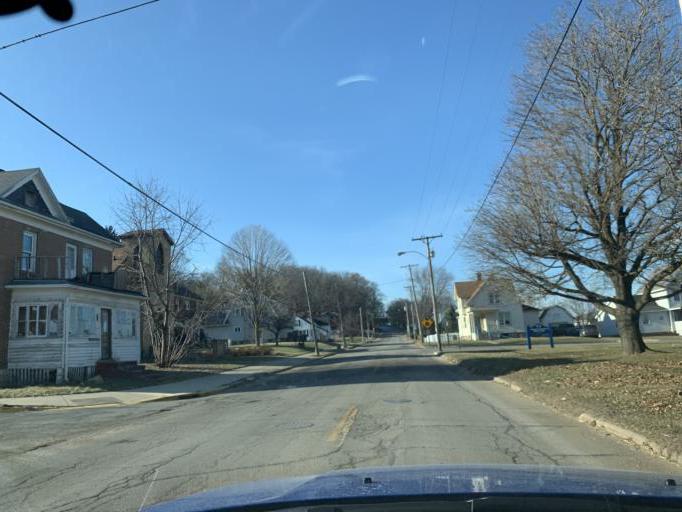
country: US
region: Wisconsin
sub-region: Iowa County
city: Barneveld
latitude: 42.8073
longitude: -89.8606
